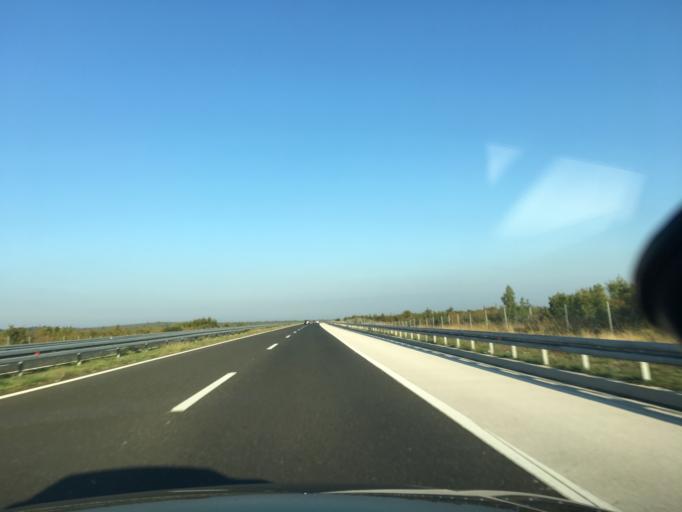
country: HR
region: Zadarska
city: Benkovac
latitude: 43.9568
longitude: 15.6731
